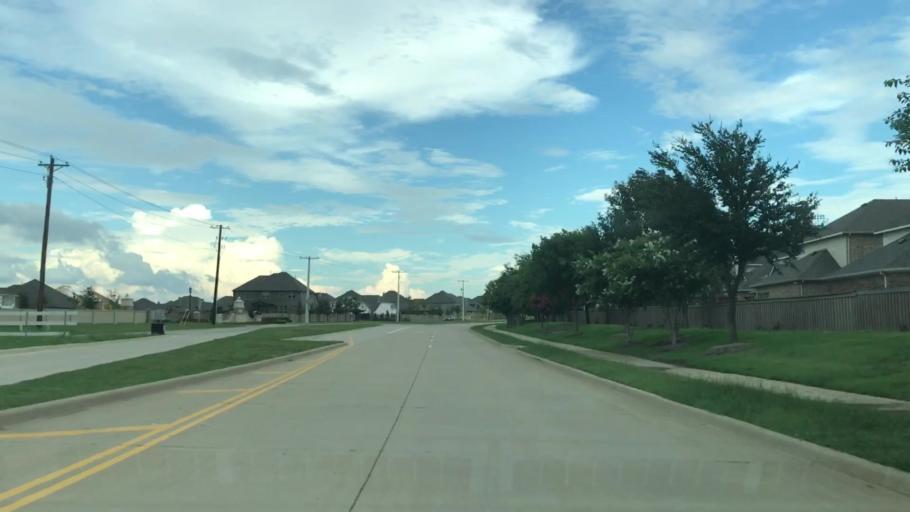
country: US
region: Texas
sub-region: Collin County
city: Prosper
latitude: 33.1880
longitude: -96.7787
